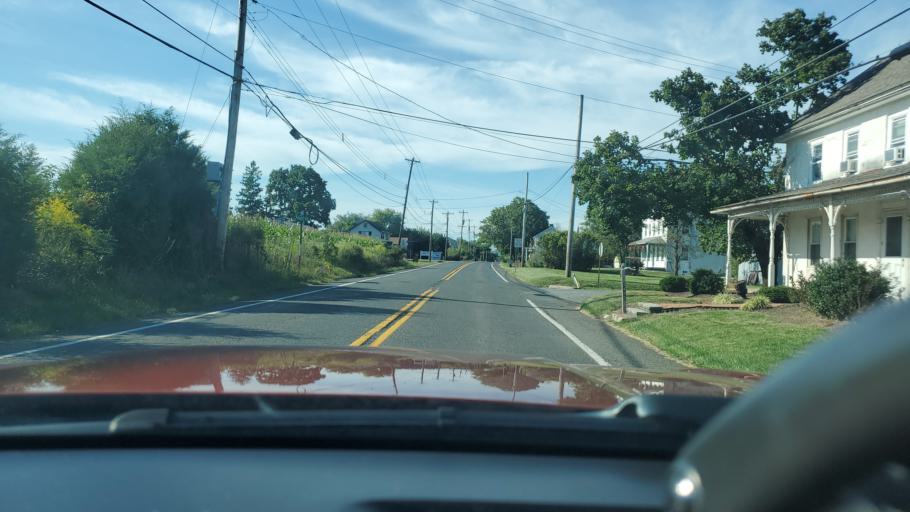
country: US
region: Pennsylvania
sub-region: Montgomery County
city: Spring Mount
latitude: 40.2877
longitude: -75.5116
